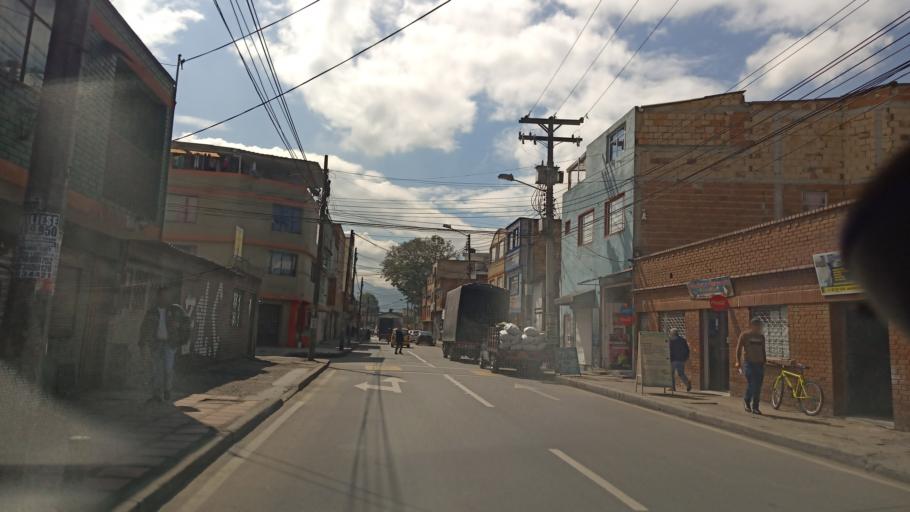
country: CO
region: Cundinamarca
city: Funza
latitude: 4.6809
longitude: -74.1379
